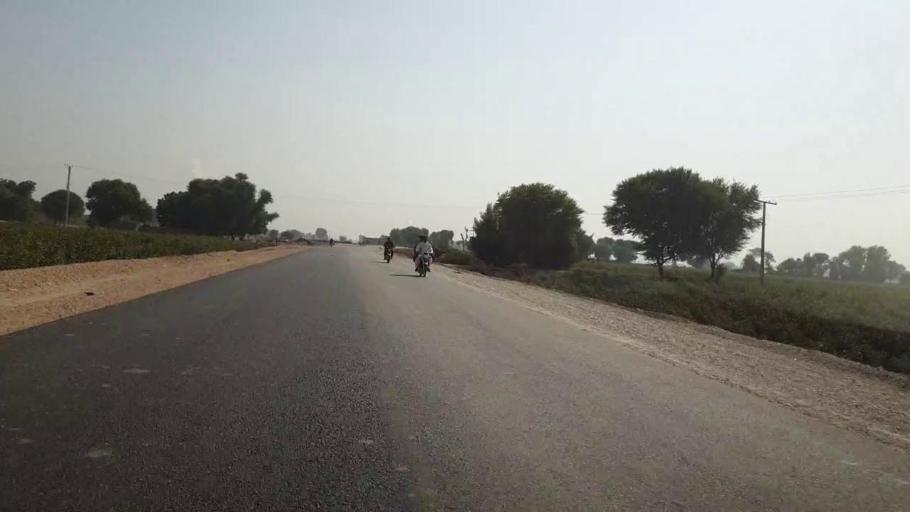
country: PK
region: Sindh
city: Dadu
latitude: 26.6782
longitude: 67.7764
